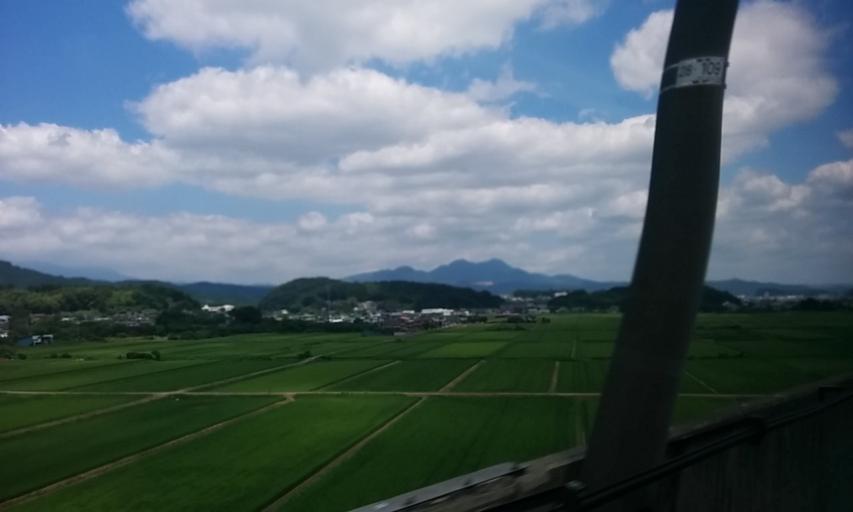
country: JP
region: Miyagi
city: Shiroishi
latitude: 37.9757
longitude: 140.6167
